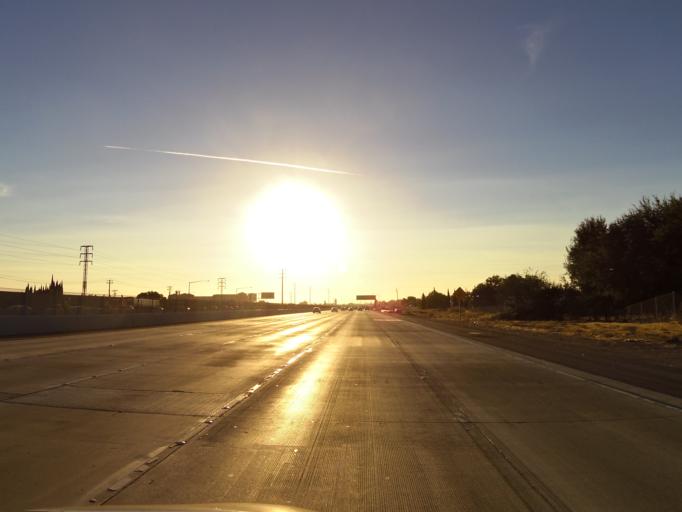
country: US
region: California
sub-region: Contra Costa County
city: Pittsburg
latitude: 38.0134
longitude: -121.8758
